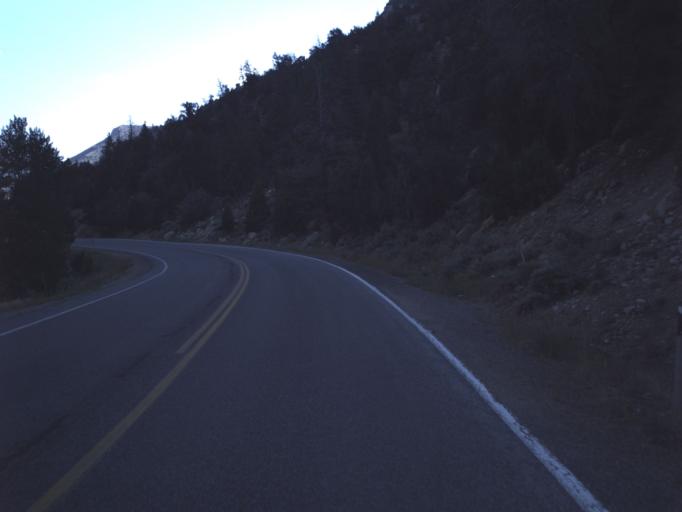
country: US
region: Utah
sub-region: Emery County
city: Huntington
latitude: 39.4327
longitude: -111.1301
